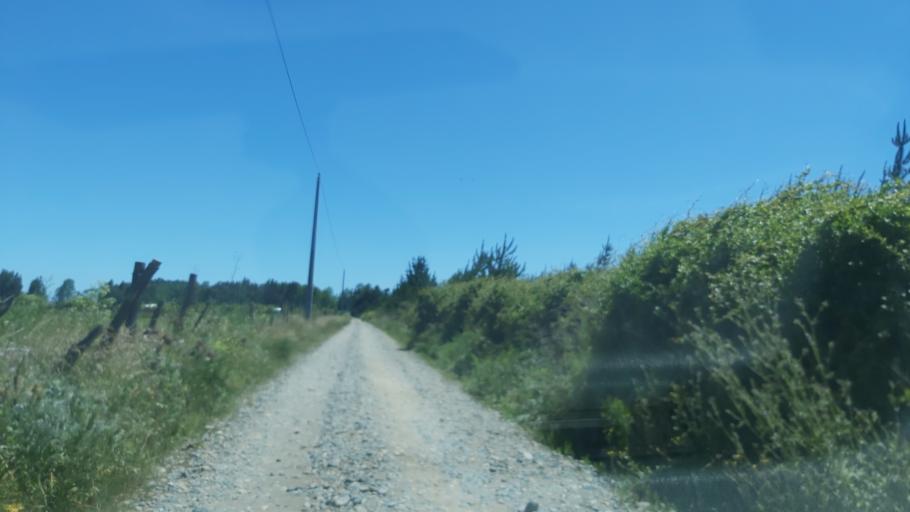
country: CL
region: Maule
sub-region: Provincia de Talca
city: Constitucion
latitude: -35.1650
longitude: -72.2636
